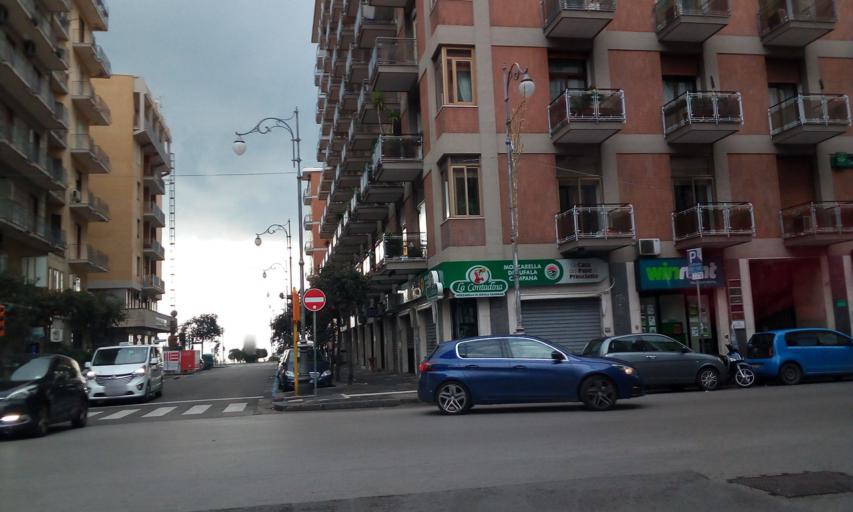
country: IT
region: Campania
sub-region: Provincia di Salerno
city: Salerno
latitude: 40.6747
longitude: 14.7715
